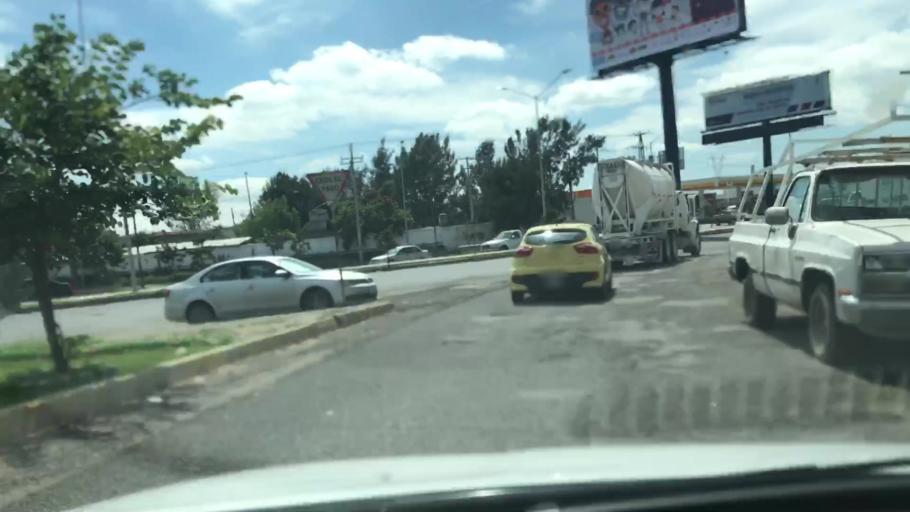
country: MX
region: Guanajuato
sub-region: Celaya
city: Roque
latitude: 20.5571
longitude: -100.8228
